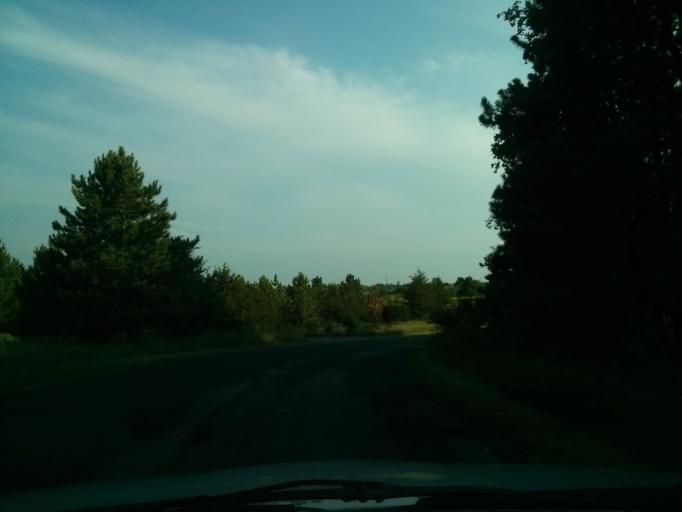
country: US
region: Wisconsin
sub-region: Saint Croix County
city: North Hudson
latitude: 45.0123
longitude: -92.6835
